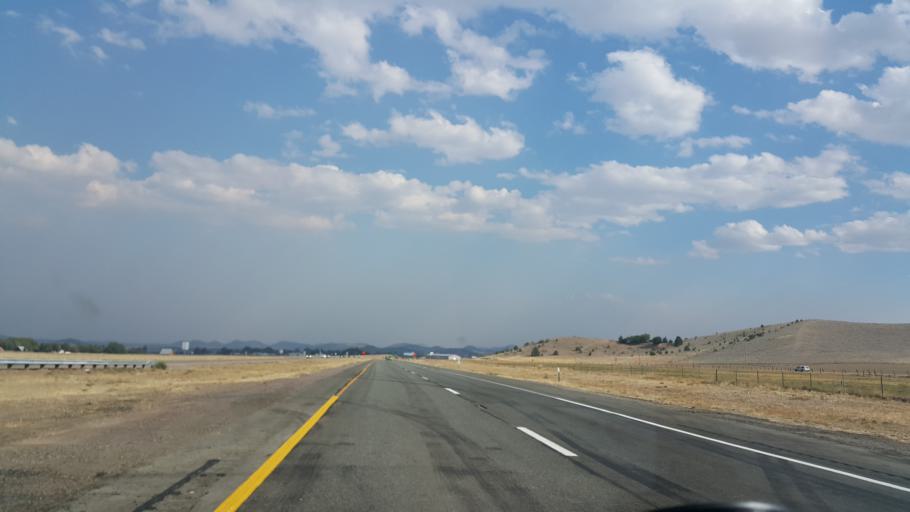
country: US
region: California
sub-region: Siskiyou County
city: Montague
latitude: 41.6519
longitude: -122.5488
